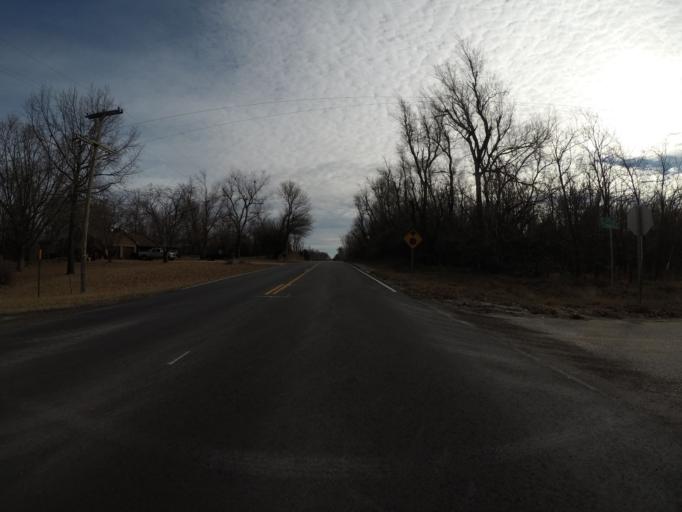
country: US
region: Kansas
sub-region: Reno County
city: Hutchinson
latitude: 38.1156
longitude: -97.8670
